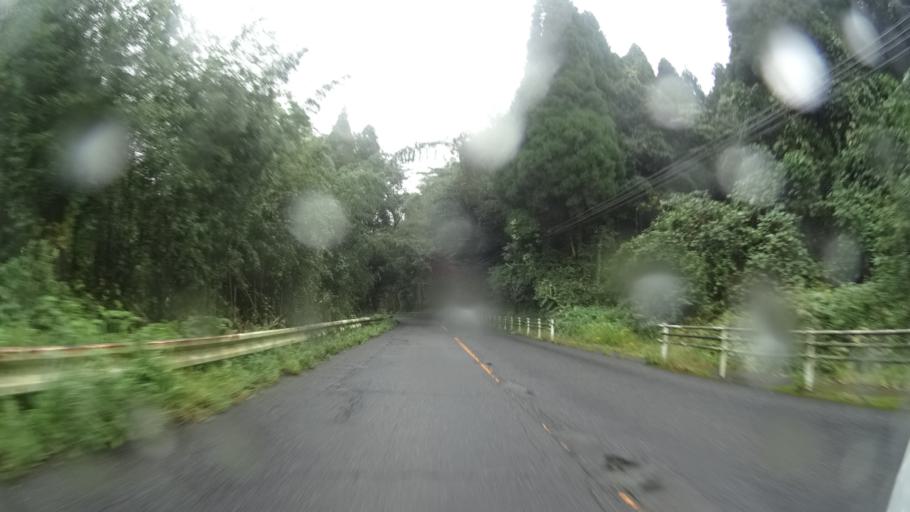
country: JP
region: Kagoshima
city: Kajiki
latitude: 31.8264
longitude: 130.6808
